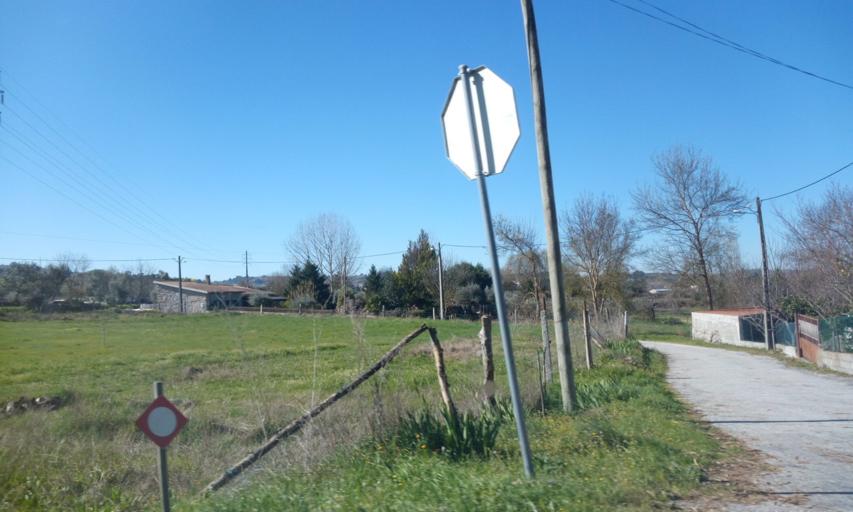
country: PT
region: Guarda
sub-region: Fornos de Algodres
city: Fornos de Algodres
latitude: 40.5308
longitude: -7.5597
